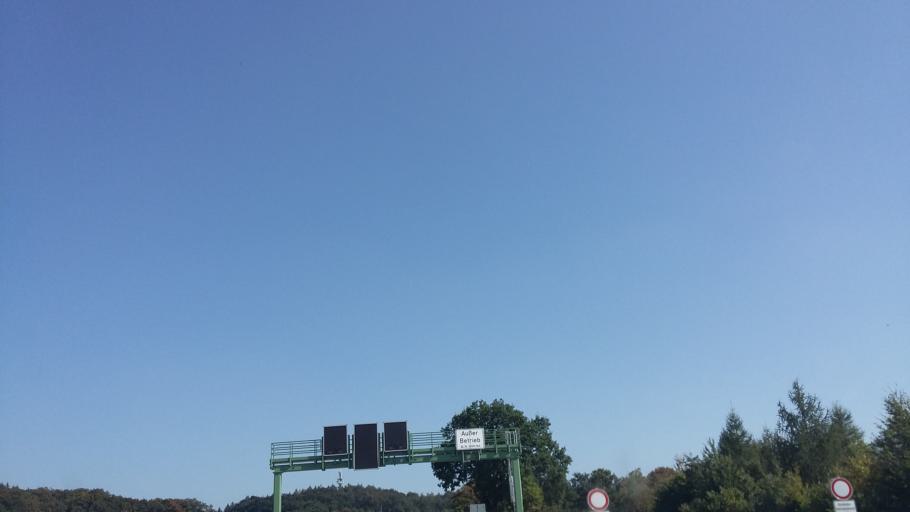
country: DE
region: Bavaria
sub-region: Upper Bavaria
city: Inning am Ammersee
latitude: 48.0838
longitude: 11.1608
